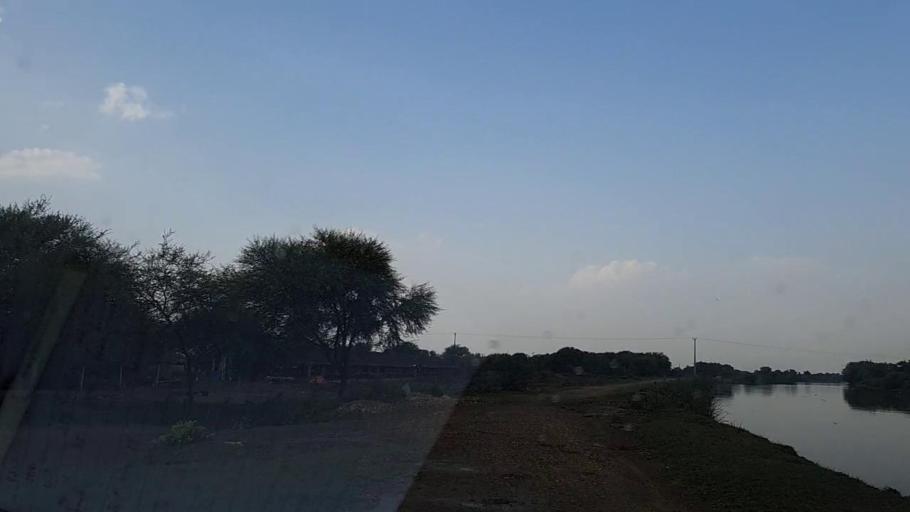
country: PK
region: Sindh
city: Daro Mehar
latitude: 24.7362
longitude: 68.1551
